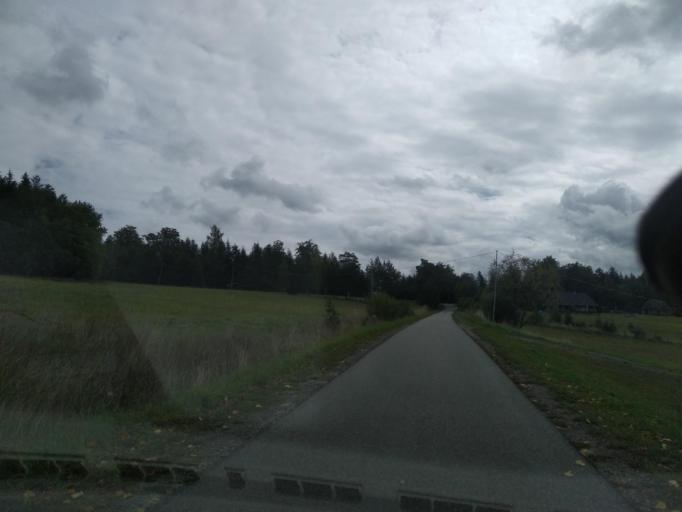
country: PL
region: Lesser Poland Voivodeship
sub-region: Powiat gorlicki
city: Uscie Gorlickie
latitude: 49.5342
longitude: 21.1738
